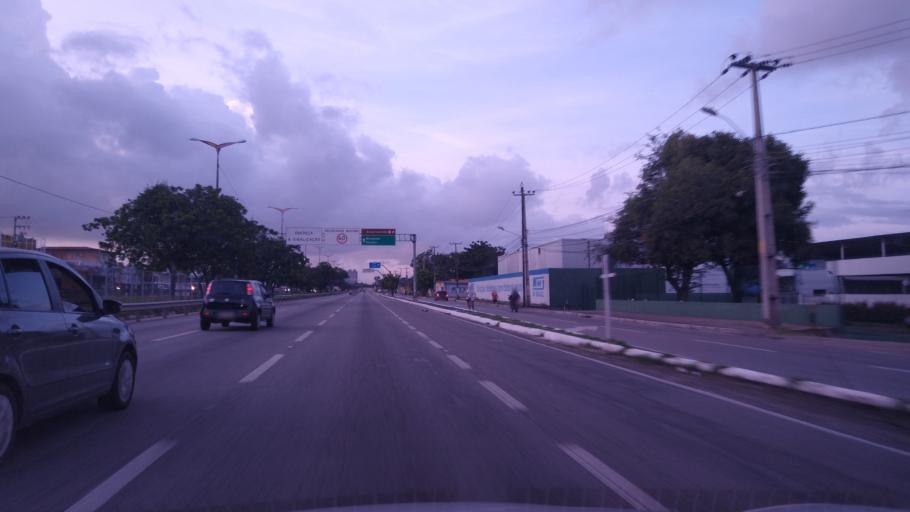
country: BR
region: Ceara
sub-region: Fortaleza
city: Fortaleza
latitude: -3.7965
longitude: -38.5069
